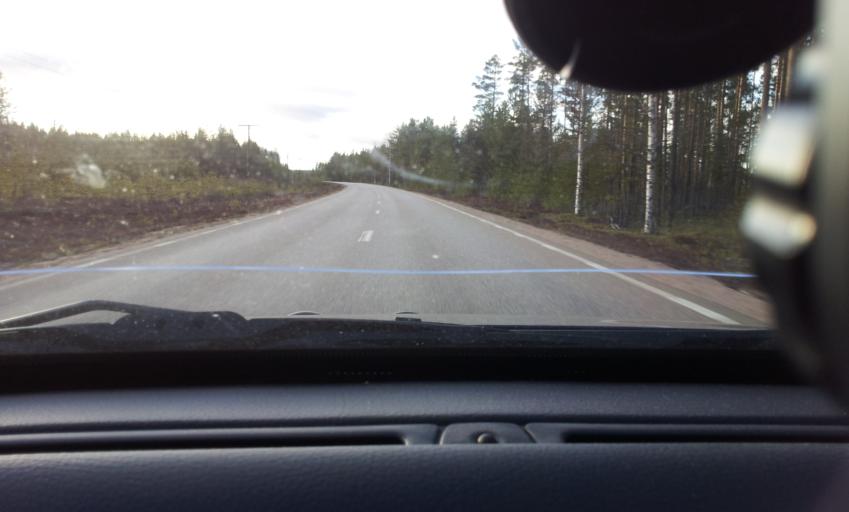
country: SE
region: Jaemtland
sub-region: Harjedalens Kommun
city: Sveg
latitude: 62.1113
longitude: 15.0586
